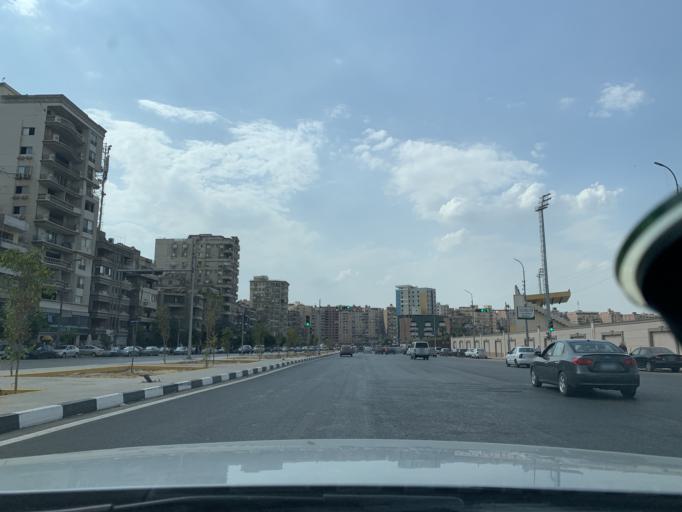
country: EG
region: Muhafazat al Qalyubiyah
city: Al Khankah
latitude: 30.1150
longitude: 31.3433
